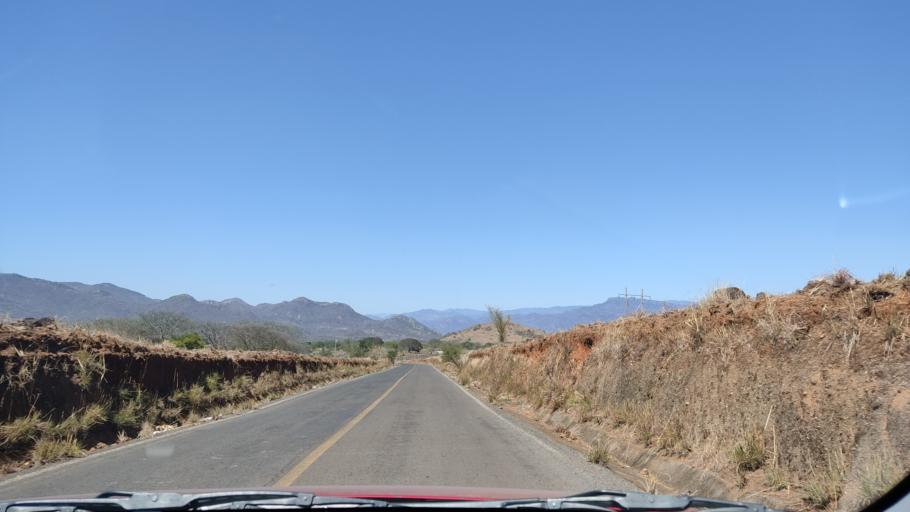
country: MX
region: Nayarit
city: Santa Maria del Oro
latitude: 21.4902
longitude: -104.6235
